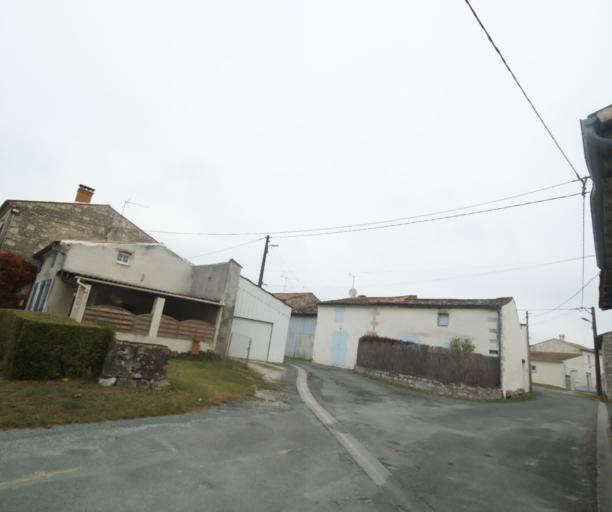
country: FR
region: Poitou-Charentes
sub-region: Departement de la Charente-Maritime
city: Saintes
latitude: 45.7588
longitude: -0.6697
